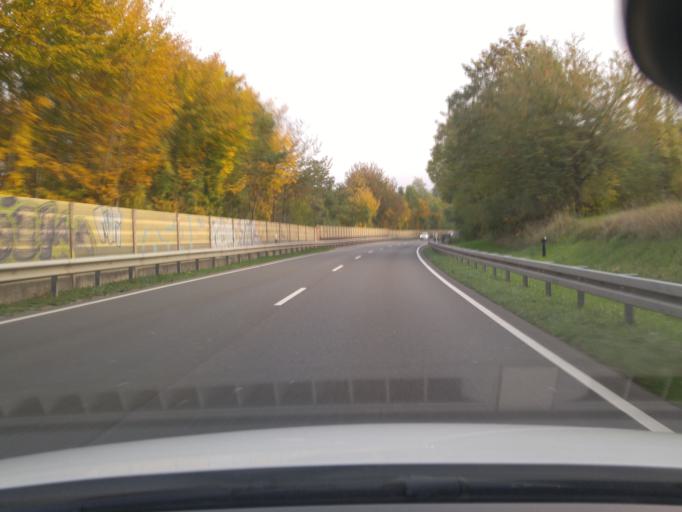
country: DE
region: Baden-Wuerttemberg
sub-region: Karlsruhe Region
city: Rauenberg
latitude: 49.2572
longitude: 8.7095
